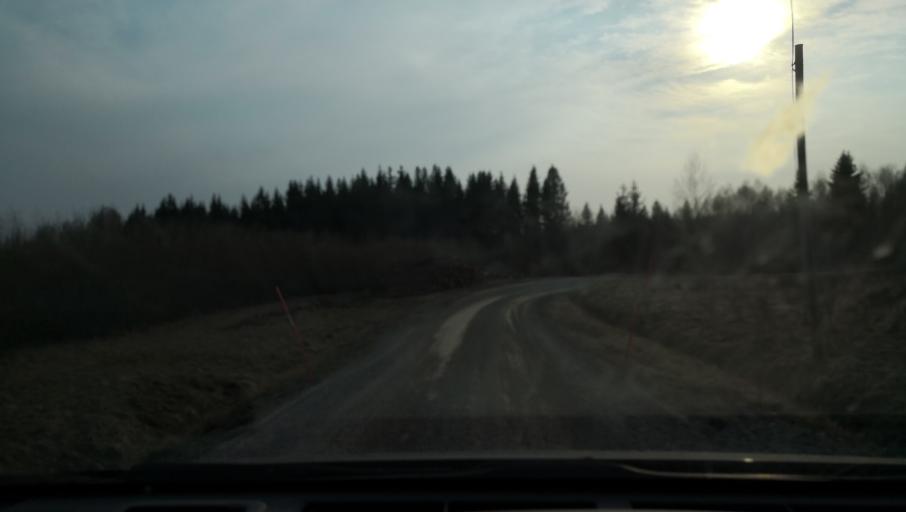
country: SE
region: OErebro
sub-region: Orebro Kommun
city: Hovsta
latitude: 59.3829
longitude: 15.2772
